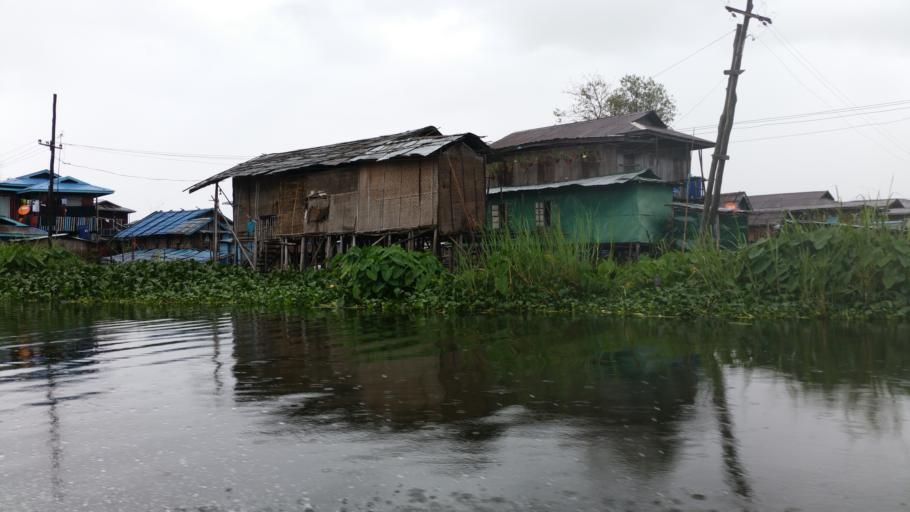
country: MM
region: Shan
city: Taunggyi
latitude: 20.5039
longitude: 96.9031
